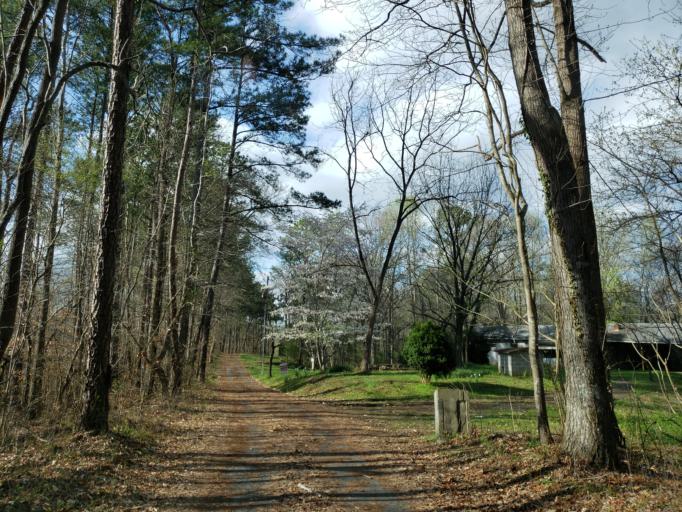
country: US
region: Georgia
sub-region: Bartow County
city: Emerson
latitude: 34.1030
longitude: -84.7442
